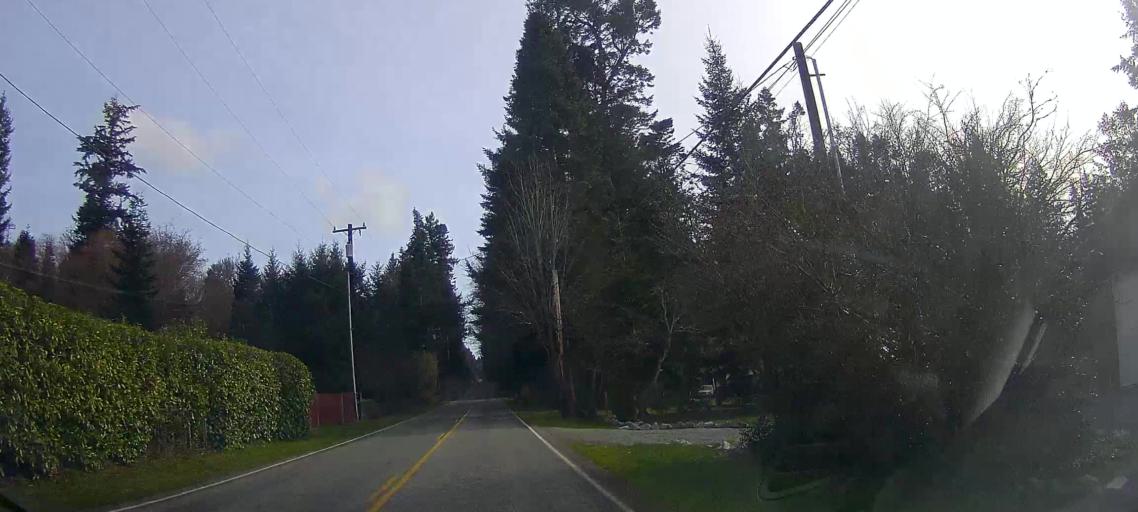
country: US
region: Washington
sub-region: Island County
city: Langley
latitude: 48.0913
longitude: -122.4062
